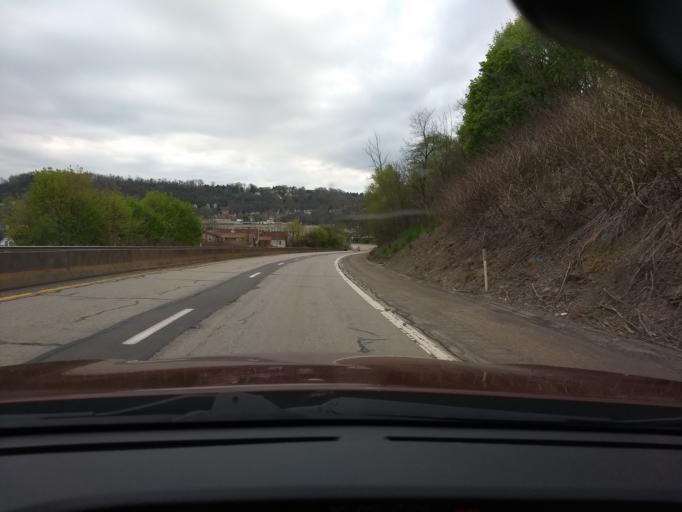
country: US
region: Pennsylvania
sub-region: Allegheny County
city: Turtle Creek
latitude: 40.4040
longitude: -79.8206
